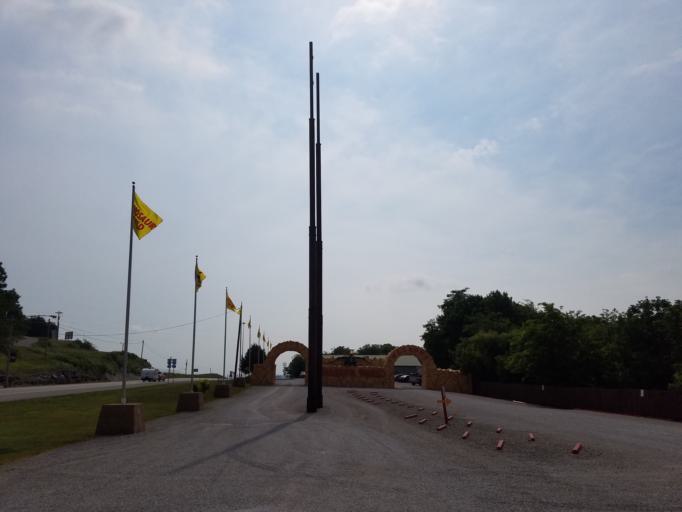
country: US
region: Kentucky
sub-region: Barren County
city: Cave City
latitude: 37.1358
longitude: -85.9828
